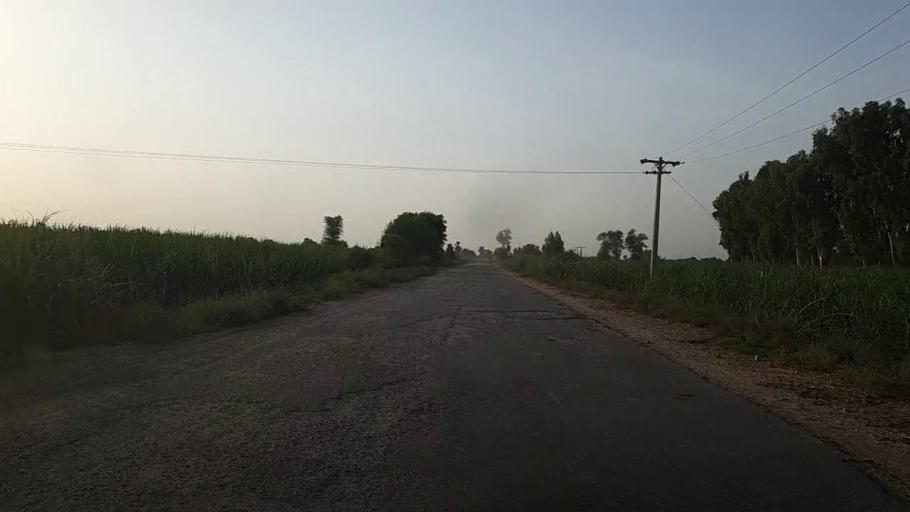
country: PK
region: Sindh
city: Ubauro
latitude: 28.1705
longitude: 69.8316
